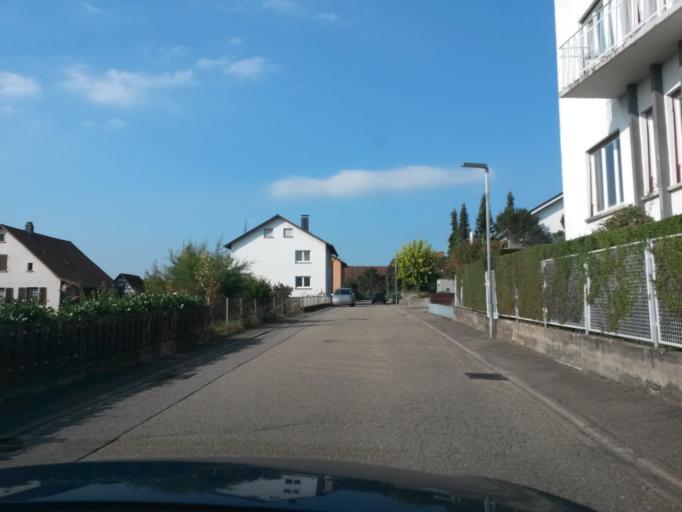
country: DE
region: Baden-Wuerttemberg
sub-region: Karlsruhe Region
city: Neuenburg
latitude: 48.9026
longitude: 8.5777
